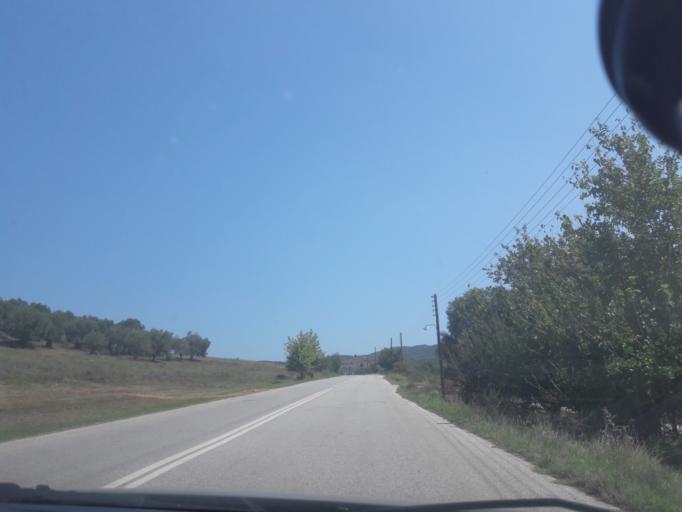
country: GR
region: Central Macedonia
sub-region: Nomos Chalkidikis
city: Megali Panagia
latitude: 40.3688
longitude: 23.6558
